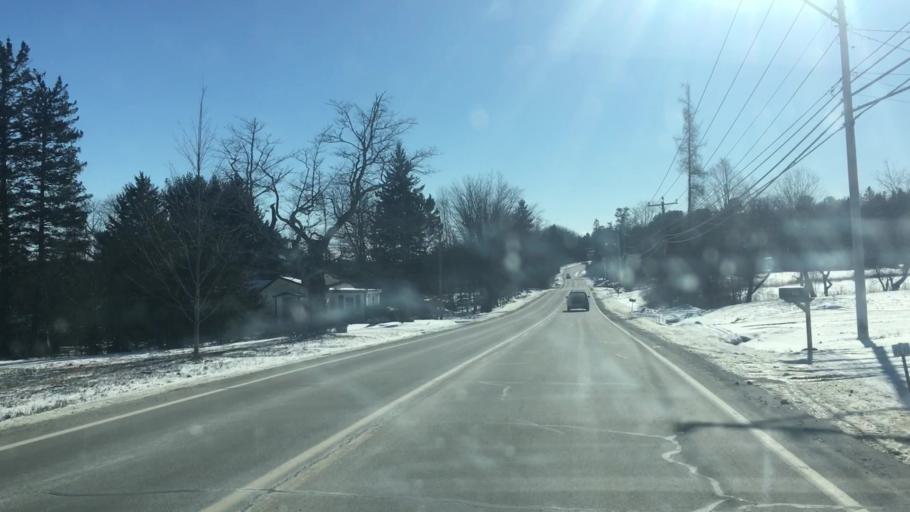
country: US
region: Maine
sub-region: Hancock County
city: Ellsworth
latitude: 44.5246
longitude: -68.4316
